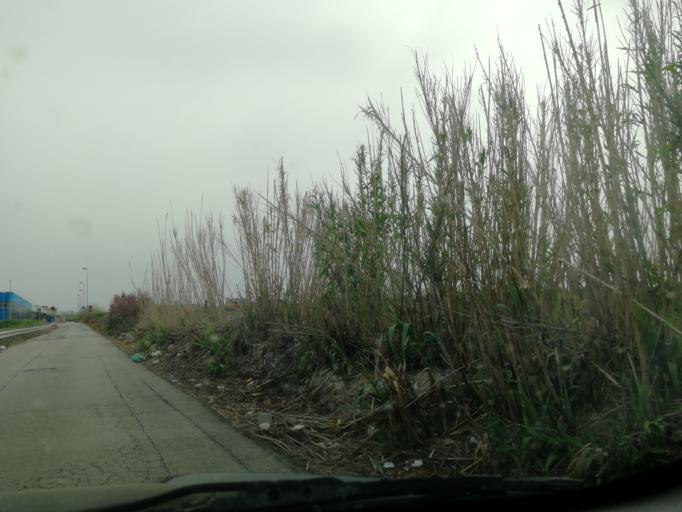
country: IT
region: Apulia
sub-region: Provincia di Barletta - Andria - Trani
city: Barletta
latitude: 41.3161
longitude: 16.3117
